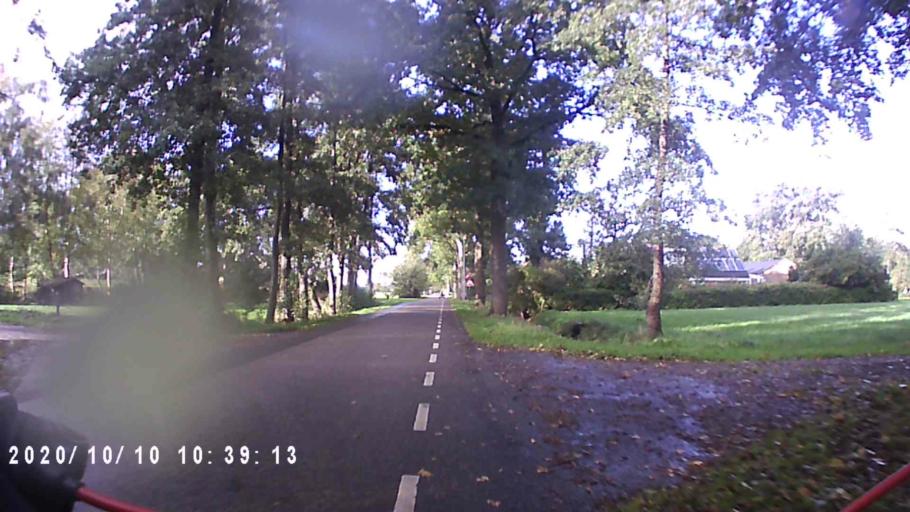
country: NL
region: Groningen
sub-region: Gemeente Grootegast
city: Grootegast
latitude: 53.1798
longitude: 6.2911
